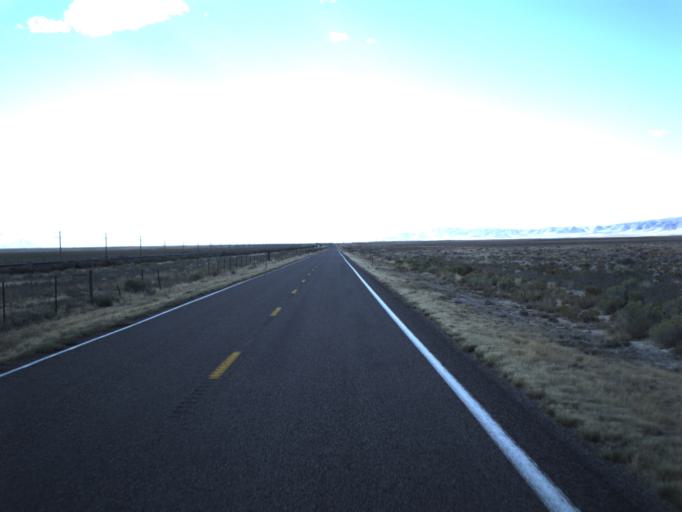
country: US
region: Utah
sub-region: Millard County
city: Delta
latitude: 39.0129
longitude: -112.7824
